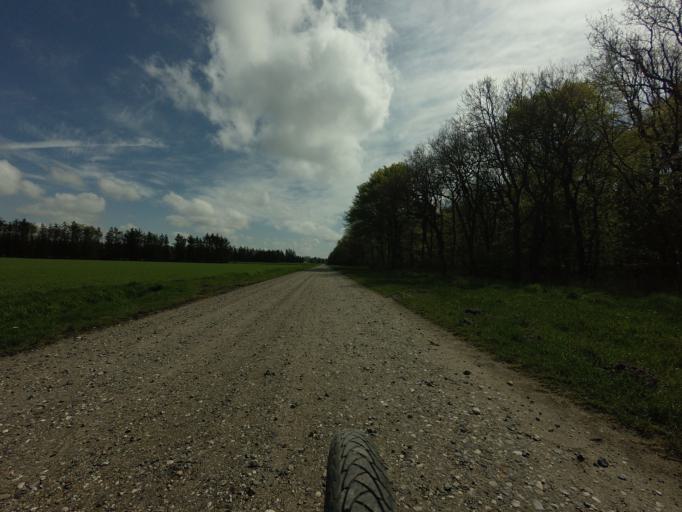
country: DK
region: North Denmark
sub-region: Jammerbugt Kommune
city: Kas
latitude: 57.1996
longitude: 9.6117
